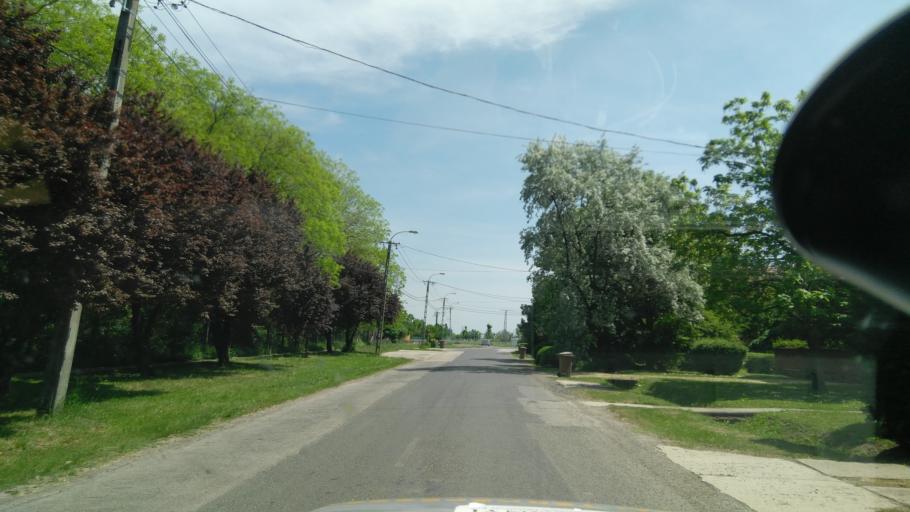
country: HU
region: Csongrad
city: Szekkutas
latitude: 46.5799
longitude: 20.4879
